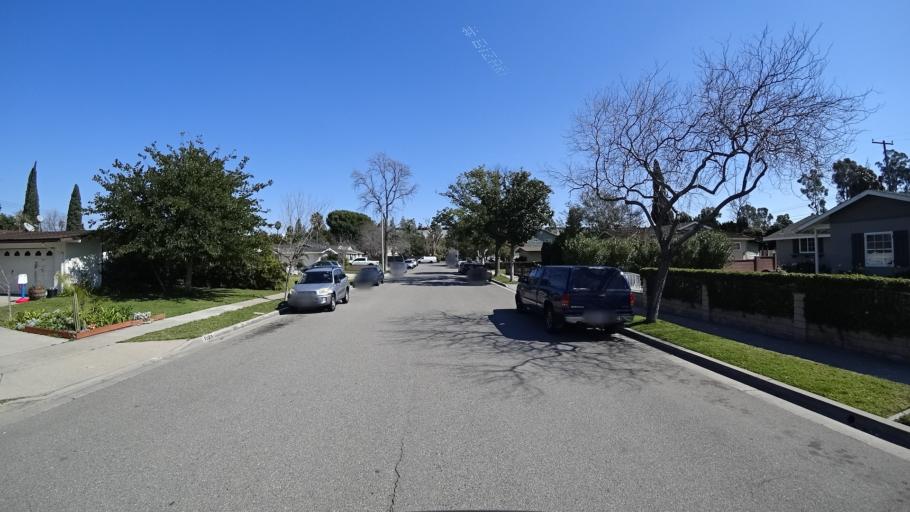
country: US
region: California
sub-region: Orange County
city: Anaheim
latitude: 33.8154
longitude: -117.9306
